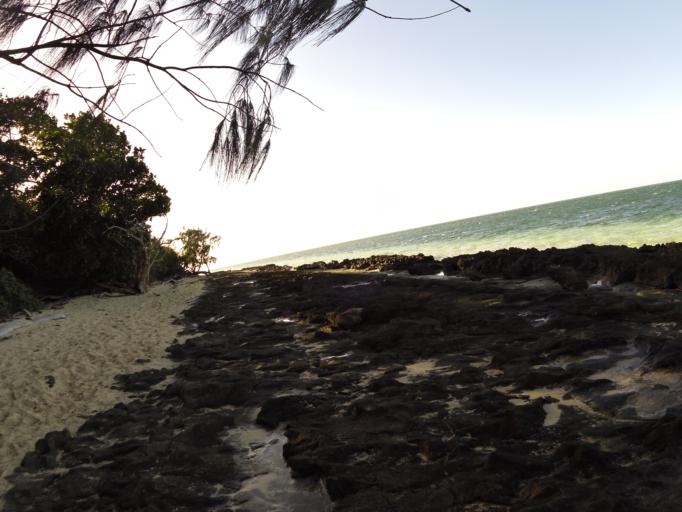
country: AU
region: Queensland
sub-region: Cairns
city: Yorkeys Knob
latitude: -16.7607
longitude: 145.9736
